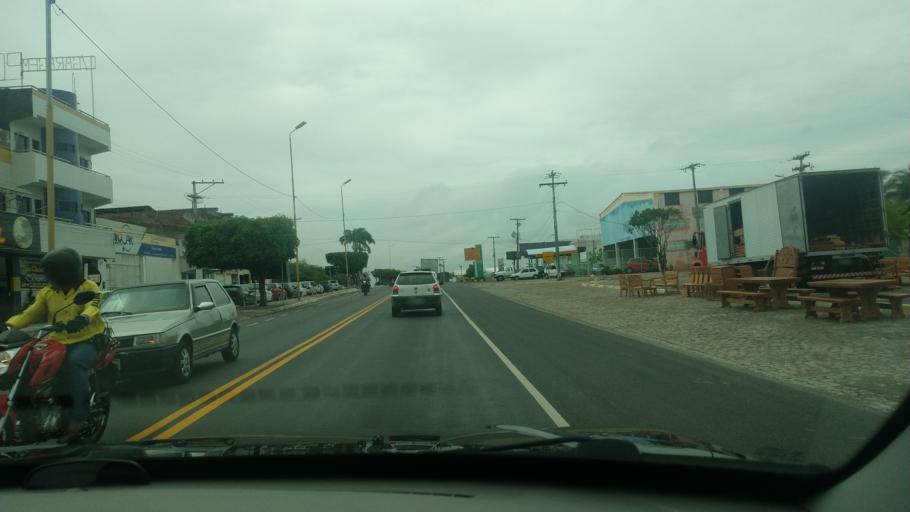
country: BR
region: Bahia
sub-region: Paulo Afonso
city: Paulo Afonso
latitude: -9.4091
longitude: -38.2362
